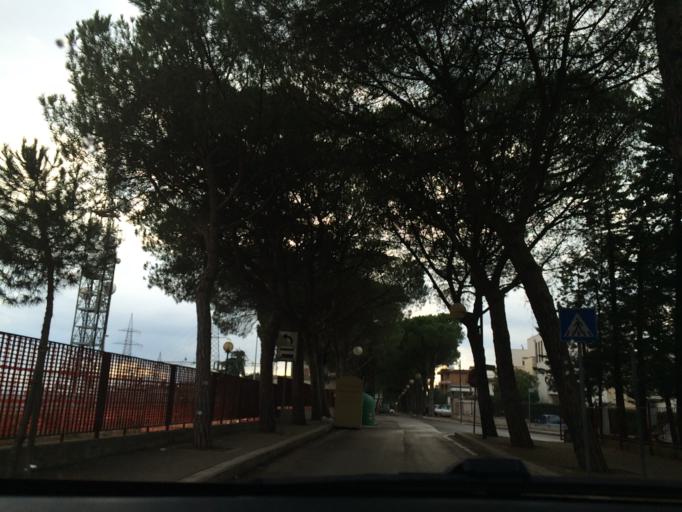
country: IT
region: Basilicate
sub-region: Provincia di Matera
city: Matera
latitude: 40.6614
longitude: 16.5988
